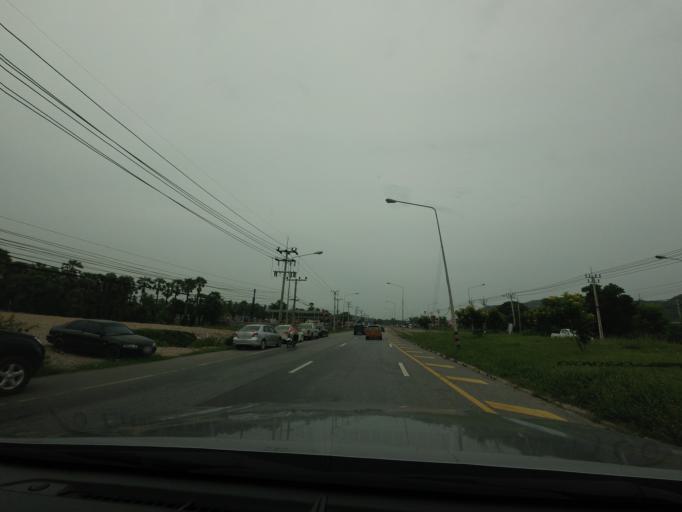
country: TH
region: Songkhla
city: Ban Mai
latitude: 7.2050
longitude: 100.5546
